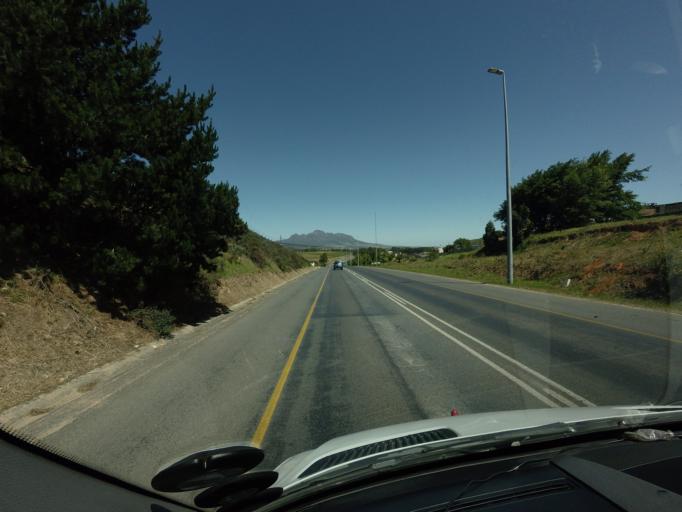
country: ZA
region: Western Cape
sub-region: Cape Winelands District Municipality
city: Stellenbosch
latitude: -33.9040
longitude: 18.8591
